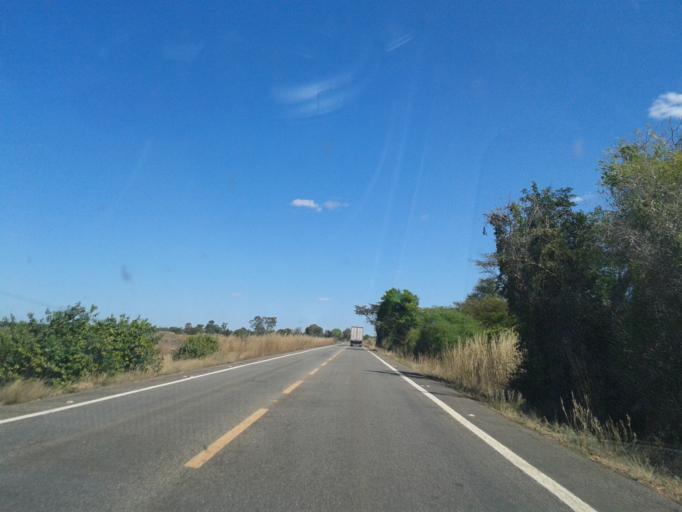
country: BR
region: Goias
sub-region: Sao Miguel Do Araguaia
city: Sao Miguel do Araguaia
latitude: -13.6052
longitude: -50.3203
